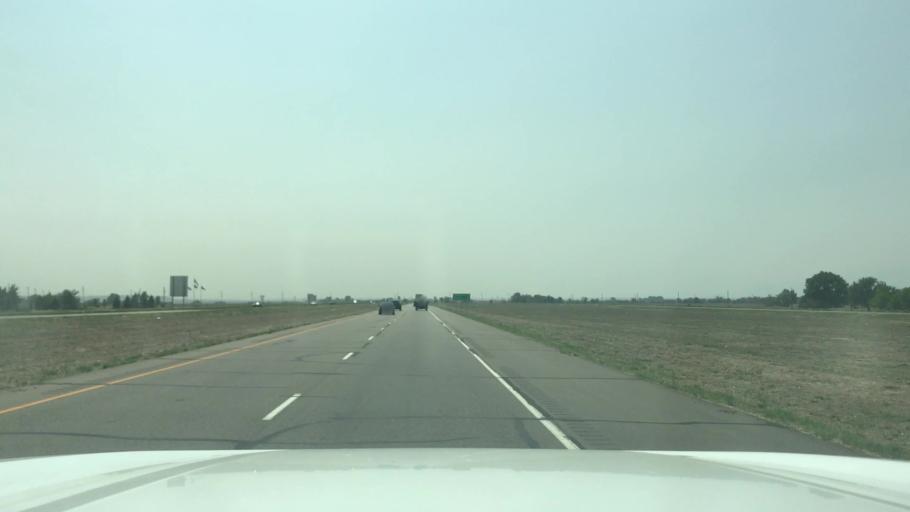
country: US
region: Colorado
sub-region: Pueblo County
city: Pueblo
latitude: 38.2061
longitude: -104.6297
